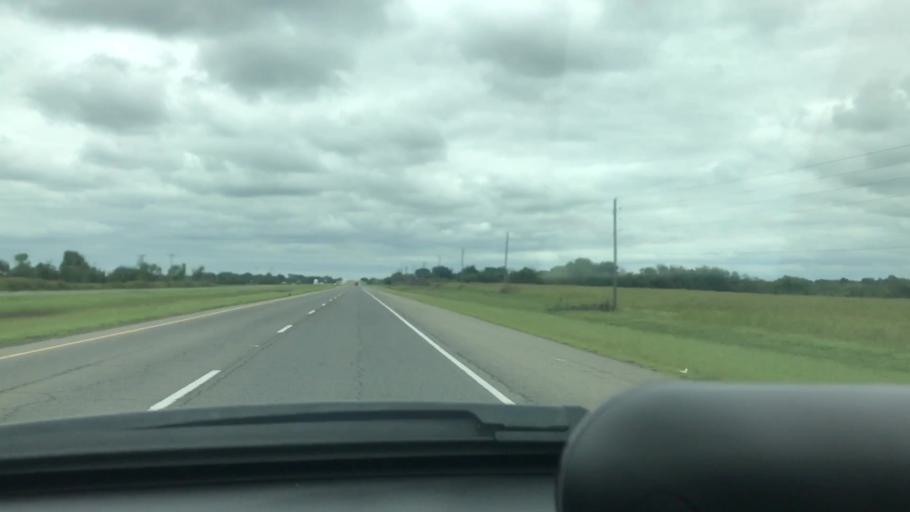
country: US
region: Oklahoma
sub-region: Wagoner County
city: Wagoner
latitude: 35.8608
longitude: -95.4026
